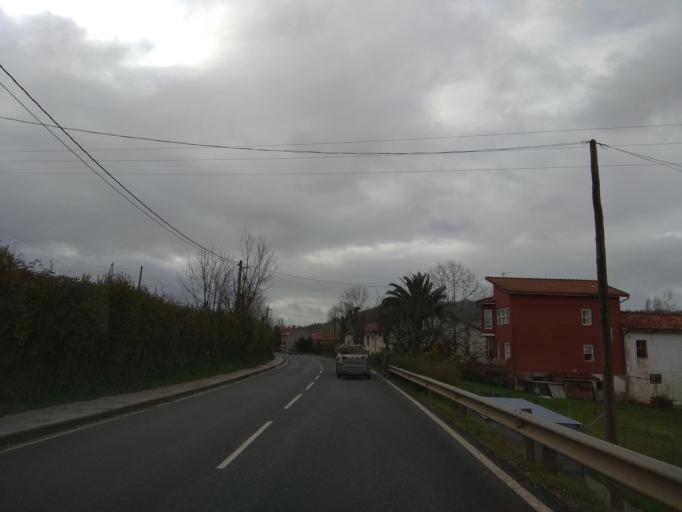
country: ES
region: Cantabria
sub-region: Provincia de Cantabria
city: Santa Maria de Cayon
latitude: 43.3302
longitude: -3.8442
